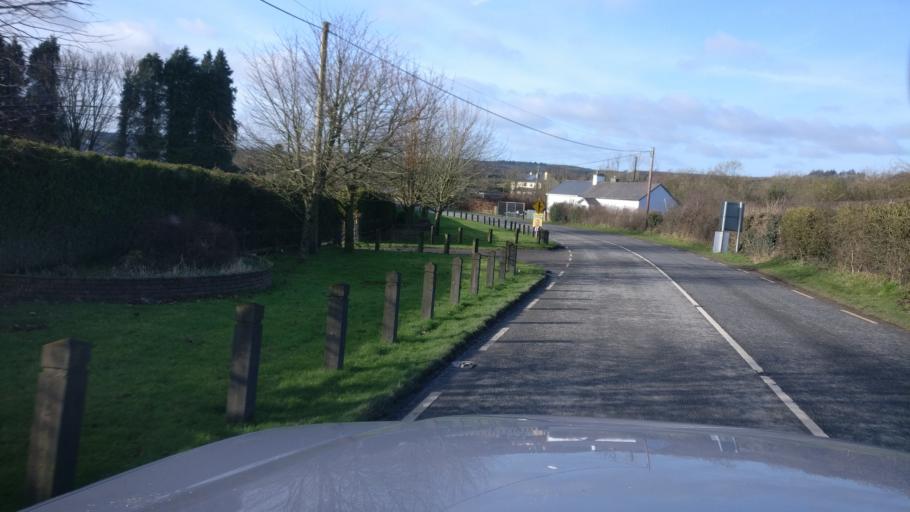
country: IE
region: Leinster
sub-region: Kilkenny
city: Castlecomer
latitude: 52.8895
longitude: -7.1613
